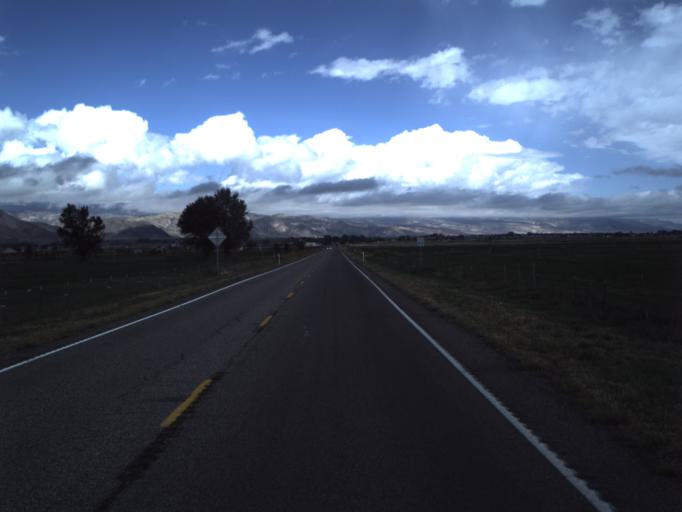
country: US
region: Utah
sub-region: Sevier County
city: Monroe
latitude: 38.6433
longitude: -112.1214
